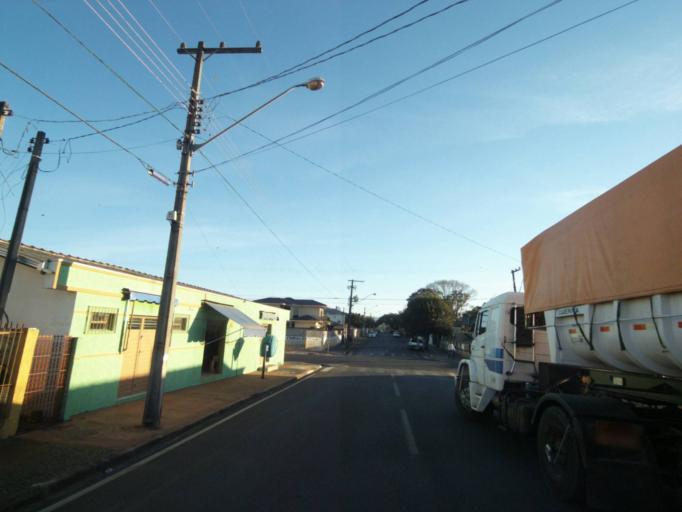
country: BR
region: Parana
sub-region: Tibagi
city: Tibagi
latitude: -24.5114
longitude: -50.4147
